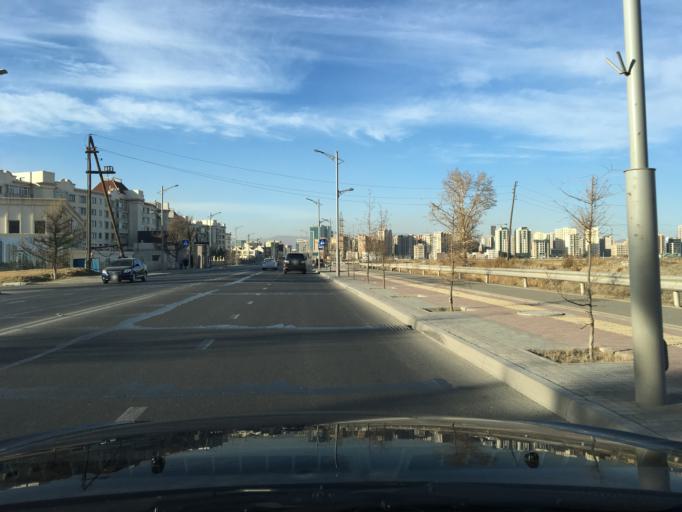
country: MN
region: Ulaanbaatar
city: Ulaanbaatar
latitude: 47.8919
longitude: 106.9376
